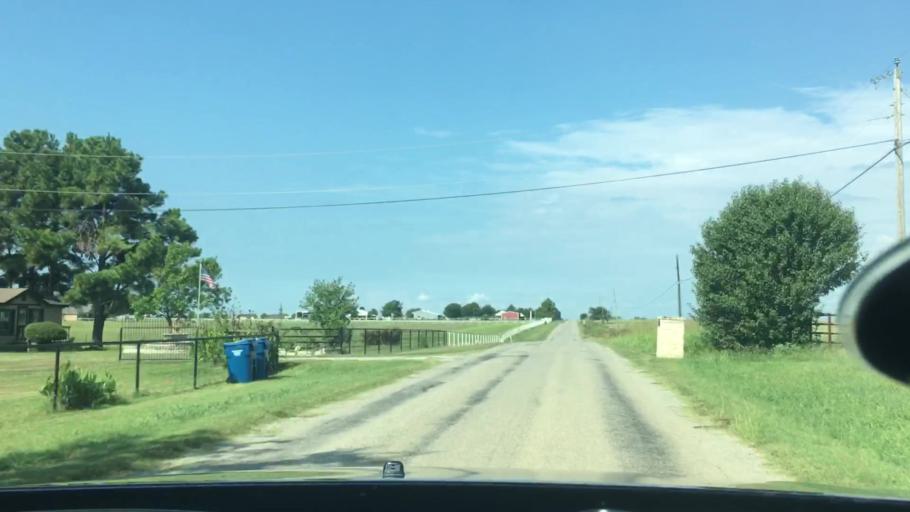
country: US
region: Oklahoma
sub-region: Bryan County
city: Colbert
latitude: 33.9110
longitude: -96.4916
